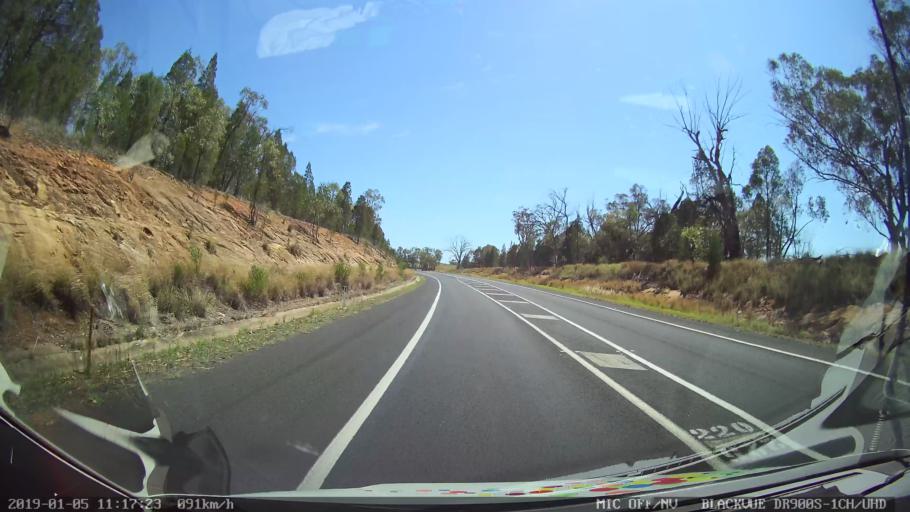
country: AU
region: New South Wales
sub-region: Warrumbungle Shire
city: Coonabarabran
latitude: -31.3273
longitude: 149.3067
